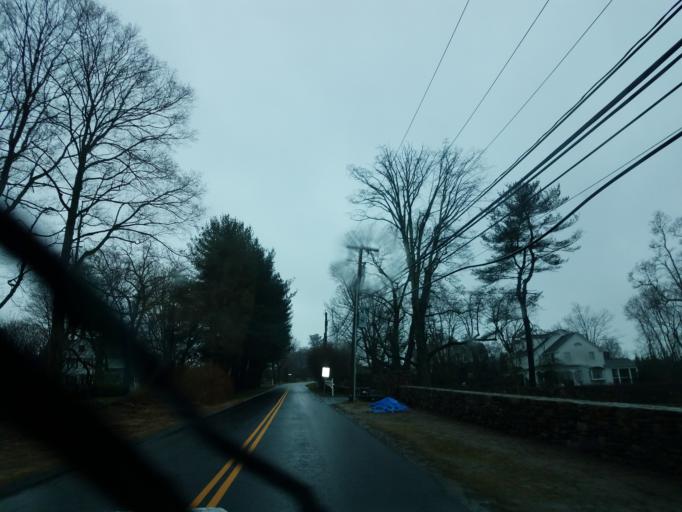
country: US
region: Connecticut
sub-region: Fairfield County
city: Southport
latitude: 41.1362
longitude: -73.3205
